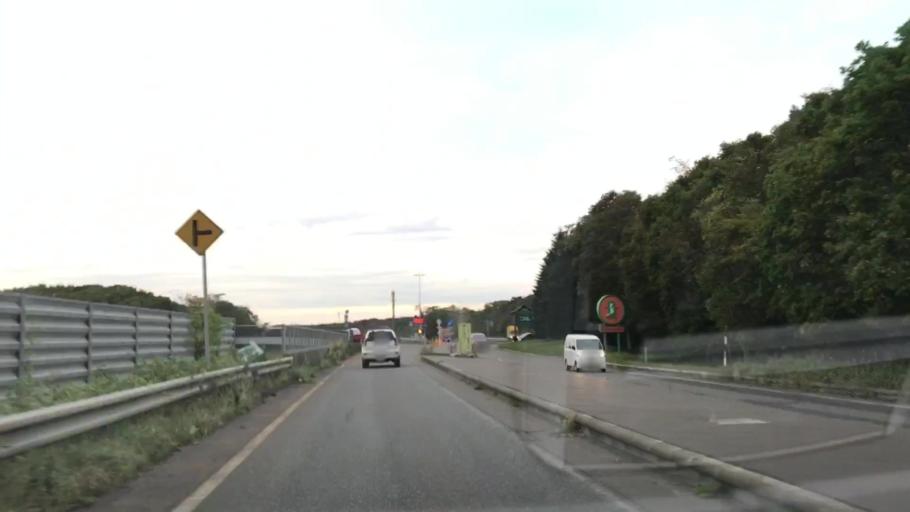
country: JP
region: Hokkaido
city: Tomakomai
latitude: 42.7071
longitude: 141.6611
